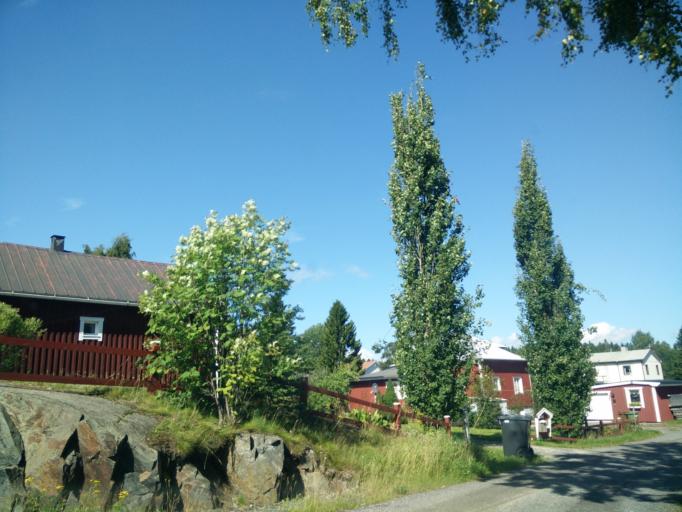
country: SE
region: Vaesternorrland
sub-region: Haernoesands Kommun
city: Haernoesand
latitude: 62.6312
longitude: 17.9067
